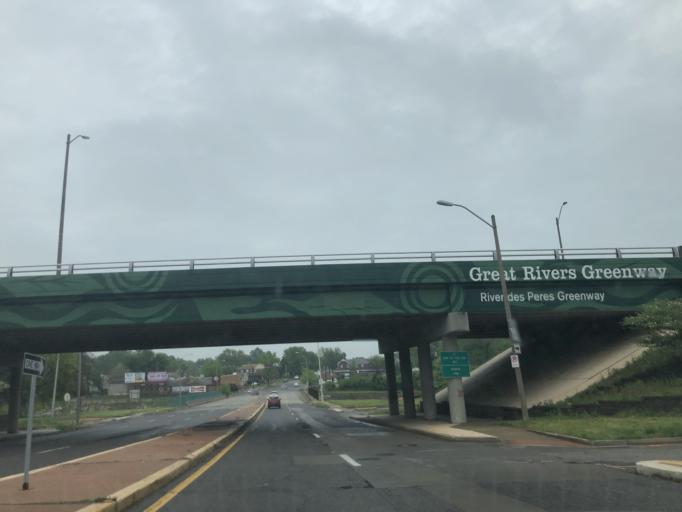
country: US
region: Missouri
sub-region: Saint Louis County
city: Shrewsbury
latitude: 38.5860
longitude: -90.3144
